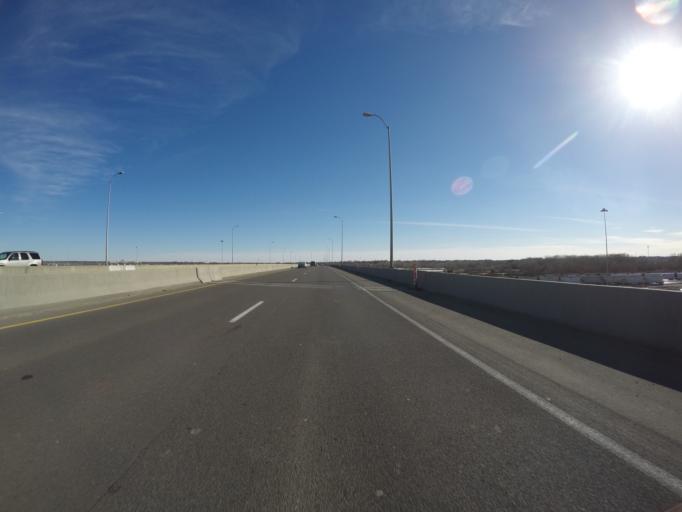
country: US
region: Nebraska
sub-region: Lancaster County
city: Lincoln
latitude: 40.8089
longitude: -96.7526
